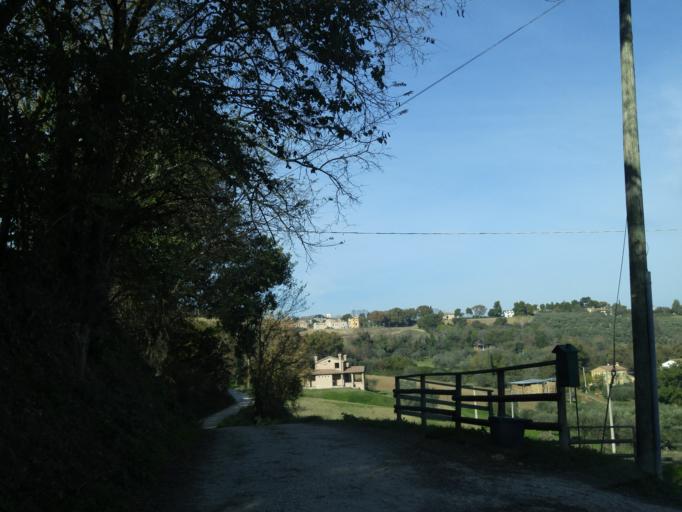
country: IT
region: The Marches
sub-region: Provincia di Pesaro e Urbino
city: Saltara
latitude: 43.7593
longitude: 12.9020
